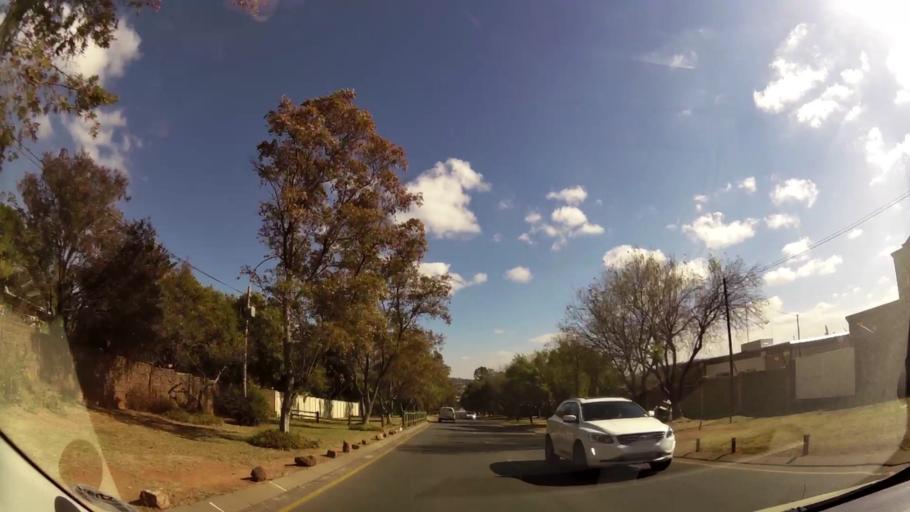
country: ZA
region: Gauteng
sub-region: City of Johannesburg Metropolitan Municipality
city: Roodepoort
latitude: -26.1049
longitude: 27.8457
